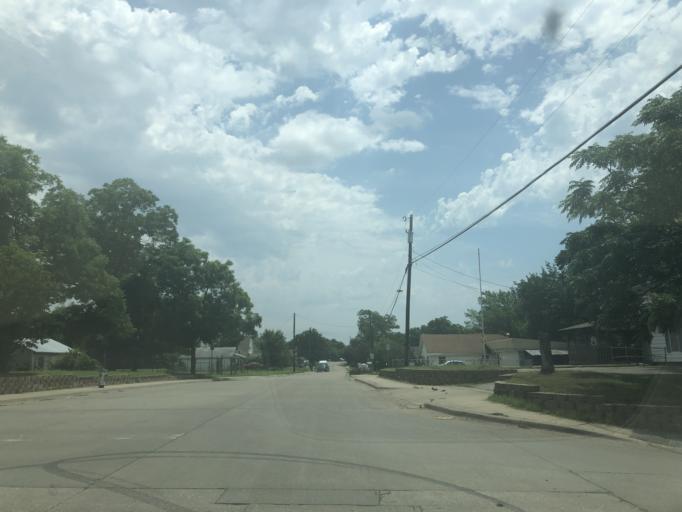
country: US
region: Texas
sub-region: Dallas County
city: Irving
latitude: 32.7939
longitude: -96.9347
